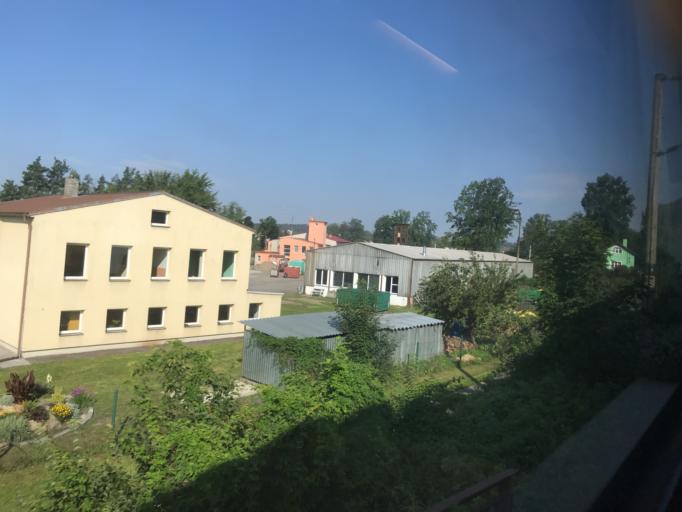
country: CZ
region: Jihocesky
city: Sobeslav
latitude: 49.2625
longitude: 14.7249
